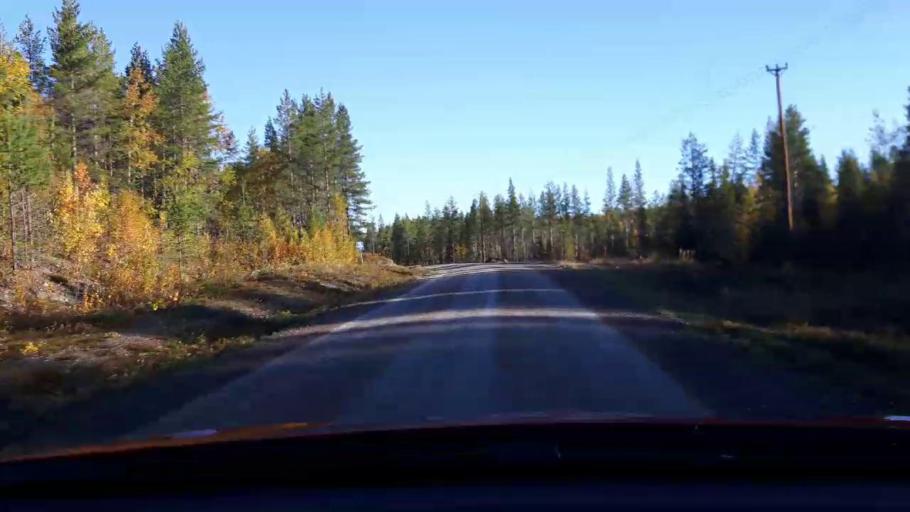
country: SE
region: Jaemtland
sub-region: Stroemsunds Kommun
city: Stroemsund
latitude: 64.3853
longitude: 15.1513
